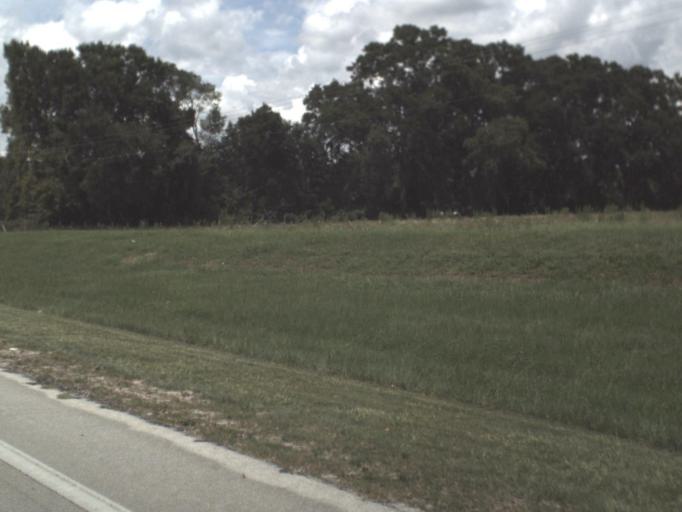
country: US
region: Florida
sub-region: Alachua County
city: High Springs
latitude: 29.7918
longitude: -82.6082
